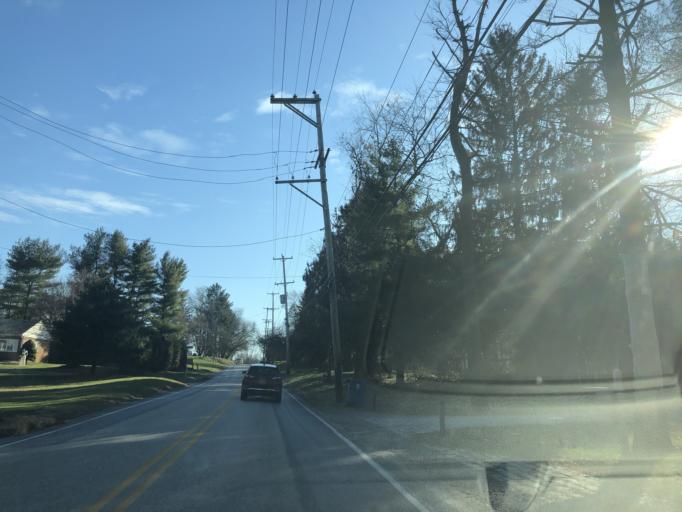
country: US
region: Pennsylvania
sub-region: Chester County
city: Toughkenamon
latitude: 39.8211
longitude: -75.7535
